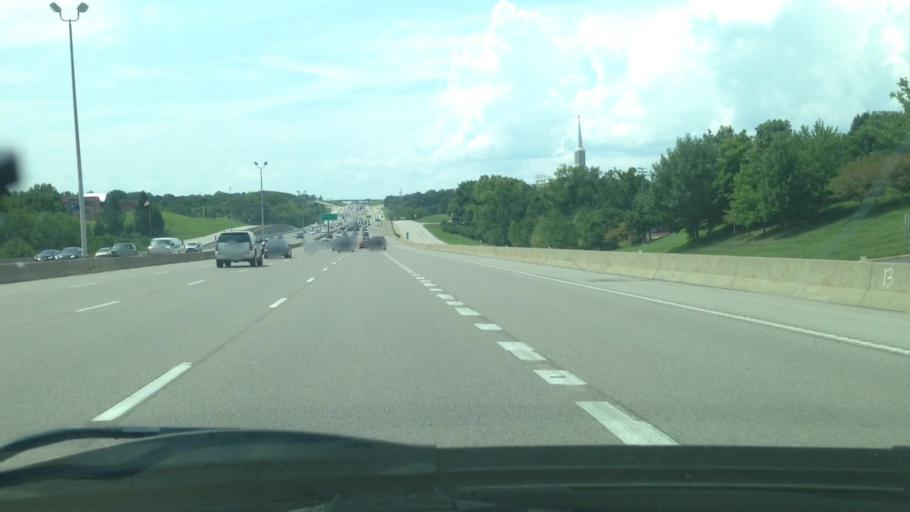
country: US
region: Missouri
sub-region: Saint Louis County
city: Town and Country
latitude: 38.6389
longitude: -90.4588
